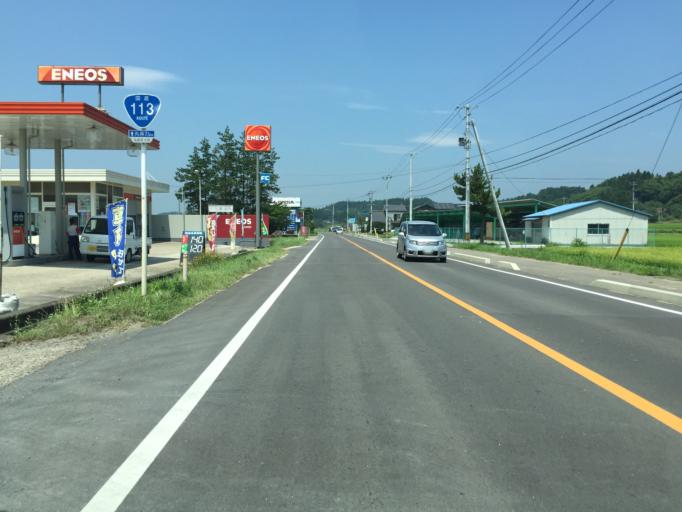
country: JP
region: Miyagi
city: Marumori
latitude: 37.8758
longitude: 140.8232
